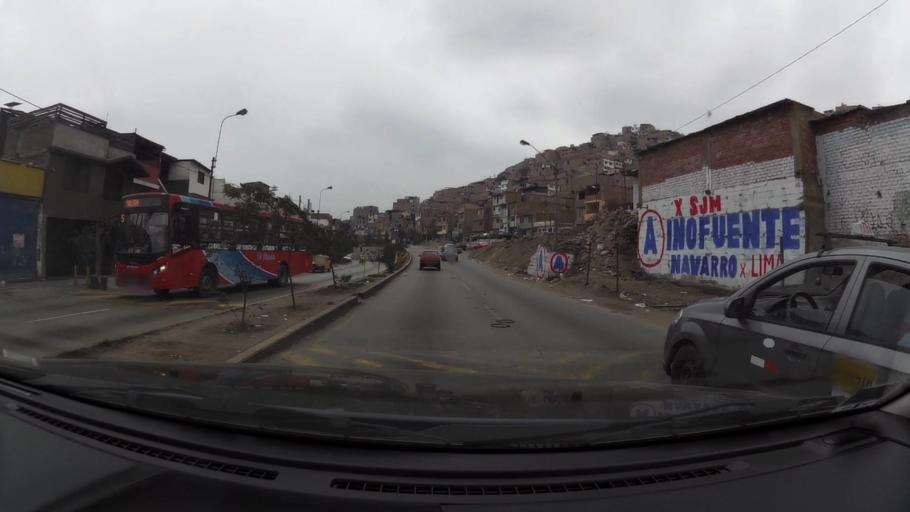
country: PE
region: Lima
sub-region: Lima
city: Surco
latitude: -12.1403
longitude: -76.9749
